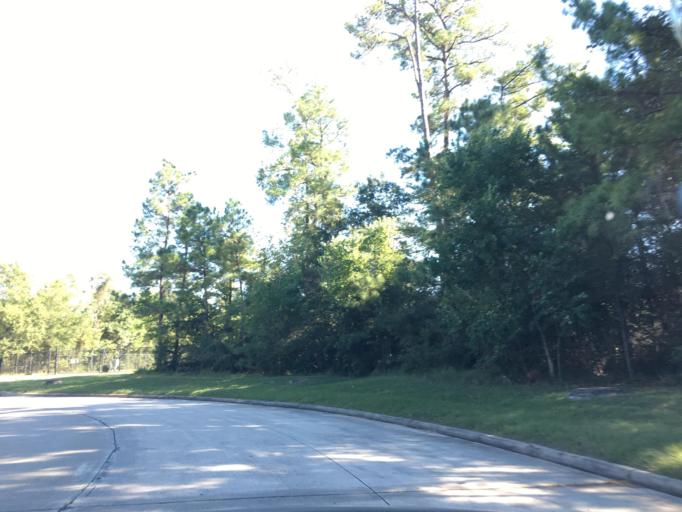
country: US
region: Texas
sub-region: Montgomery County
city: Shenandoah
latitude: 30.1998
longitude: -95.4595
